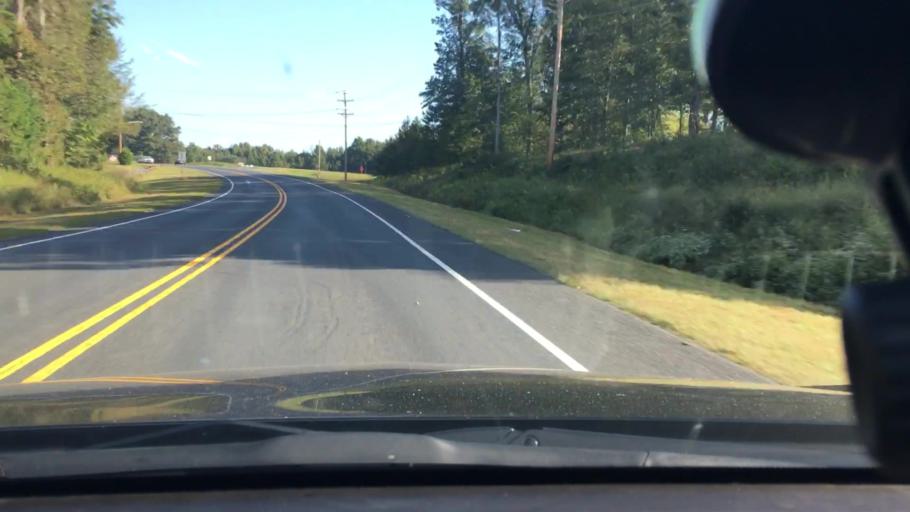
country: US
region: North Carolina
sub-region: Stanly County
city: Albemarle
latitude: 35.3664
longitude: -80.1706
